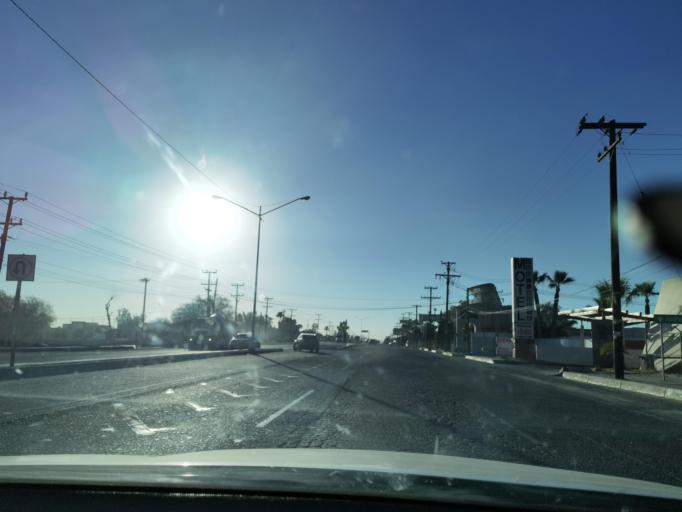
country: MX
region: Baja California
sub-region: Mexicali
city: Islas Agrarias Grupo A
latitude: 32.6529
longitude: -115.3697
